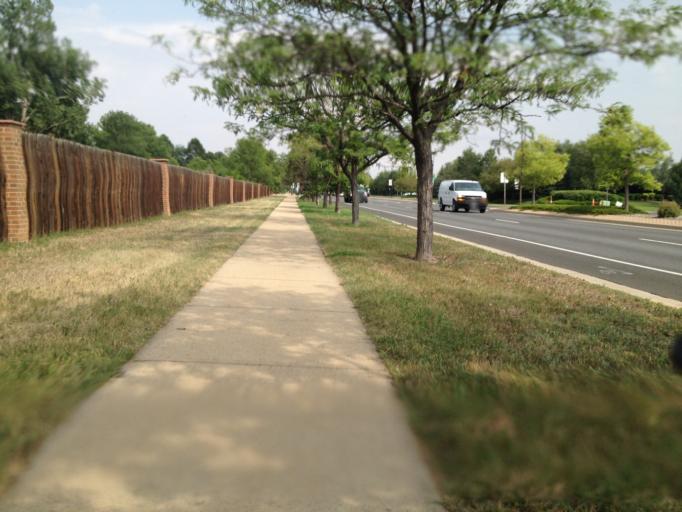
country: US
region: Colorado
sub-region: Boulder County
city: Louisville
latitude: 39.9870
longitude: -105.1608
